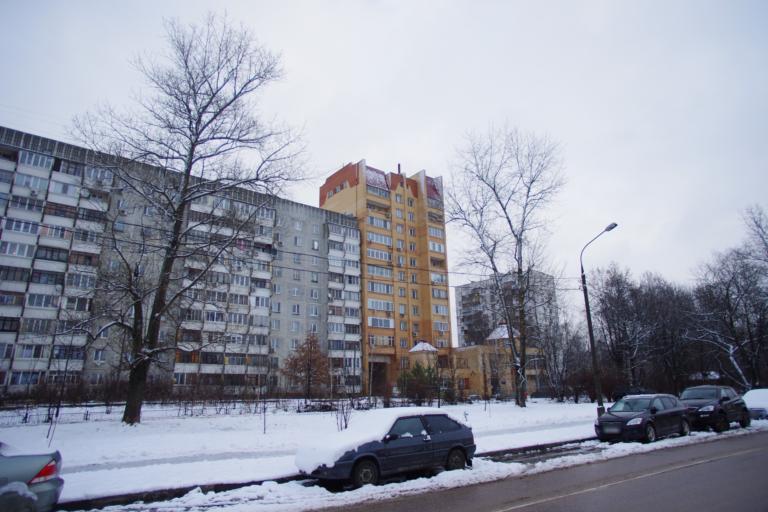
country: RU
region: Moskovskaya
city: Krasnogorsk
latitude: 55.8135
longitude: 37.3069
